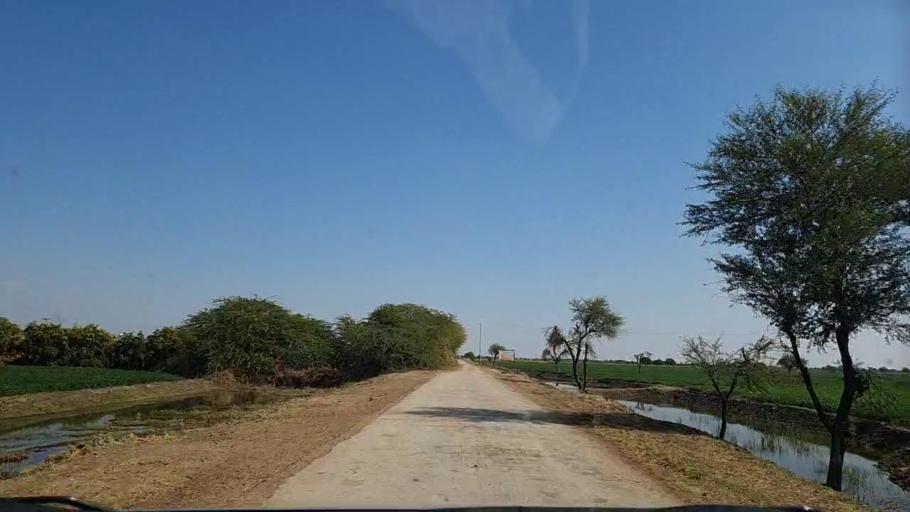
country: PK
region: Sindh
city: Pithoro
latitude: 25.6863
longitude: 69.4672
